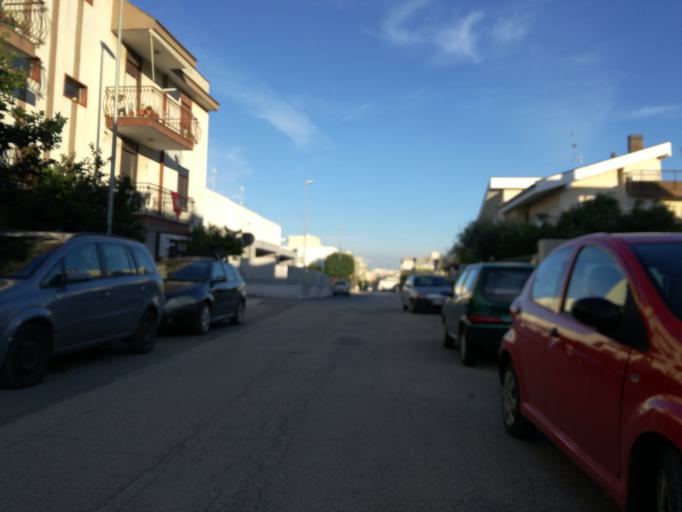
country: IT
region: Apulia
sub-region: Provincia di Bari
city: Adelfia
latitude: 40.9988
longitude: 16.8687
